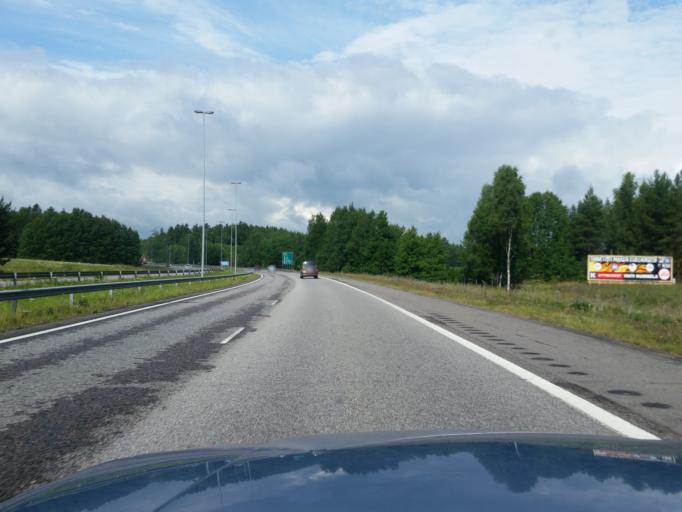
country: FI
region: Uusimaa
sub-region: Helsinki
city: Vihti
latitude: 60.2928
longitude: 24.3881
